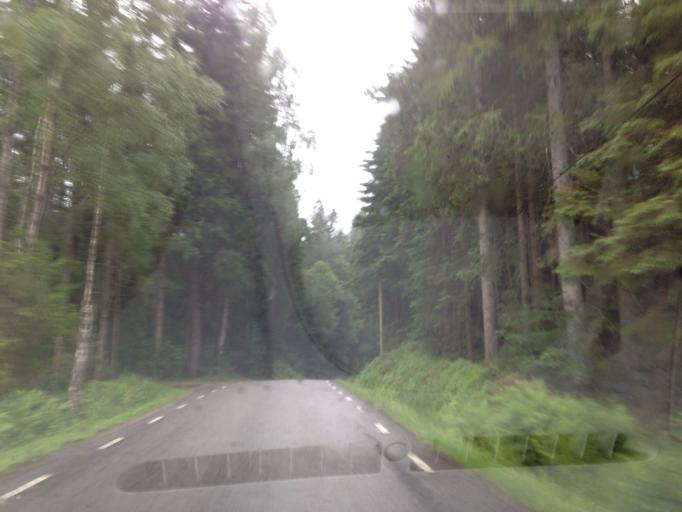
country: SE
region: Vaestra Goetaland
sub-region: Marks Kommun
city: Horred
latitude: 57.1661
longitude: 12.7353
